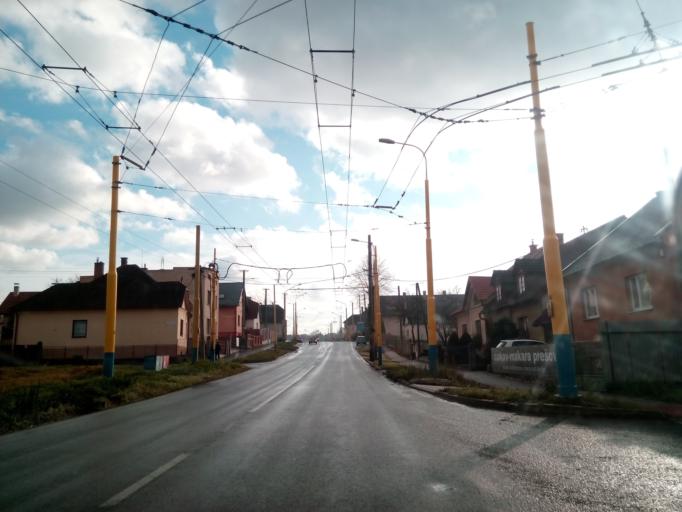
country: SK
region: Presovsky
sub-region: Okres Presov
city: Presov
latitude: 48.9792
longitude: 21.2608
